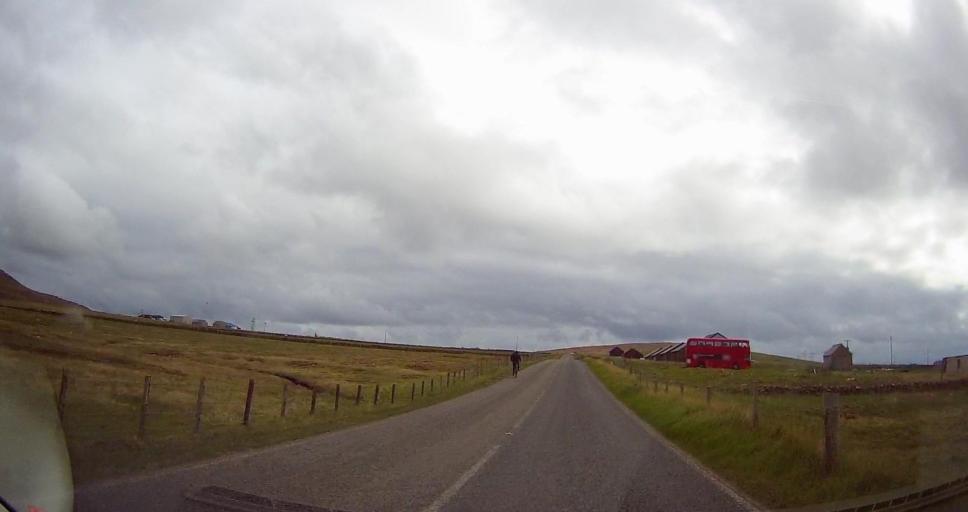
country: GB
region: Scotland
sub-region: Shetland Islands
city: Shetland
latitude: 60.7647
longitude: -0.8431
